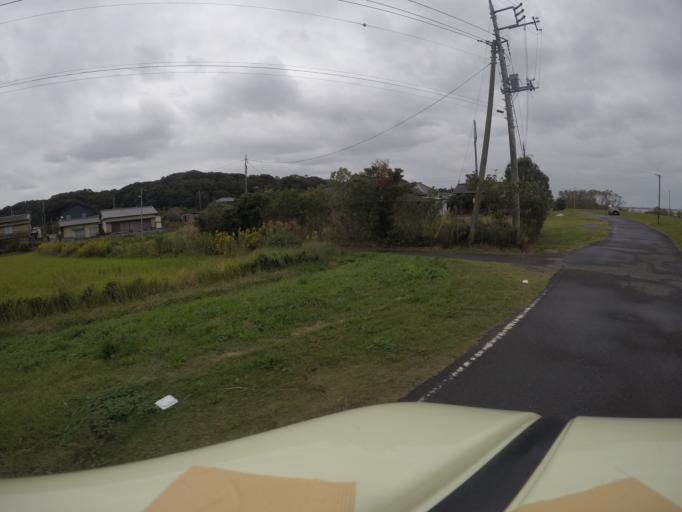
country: JP
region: Ibaraki
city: Itako
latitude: 35.9997
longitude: 140.4706
